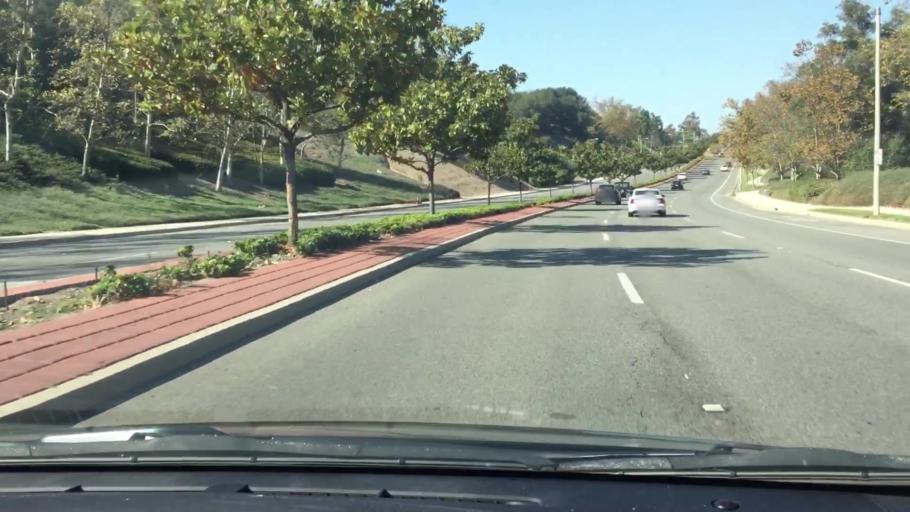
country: US
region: California
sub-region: Orange County
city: Rancho Santa Margarita
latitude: 33.6398
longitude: -117.6205
